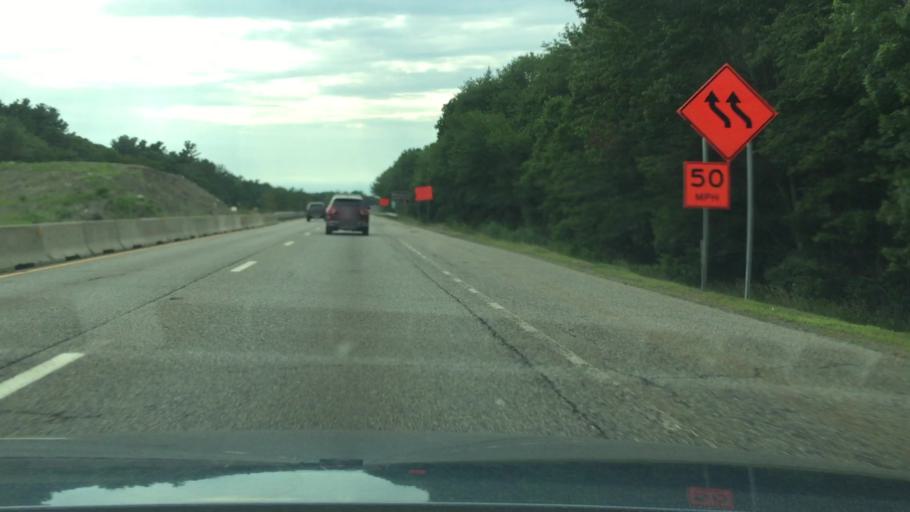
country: US
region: Massachusetts
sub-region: Plymouth County
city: Rockland
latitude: 42.1574
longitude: -70.8641
